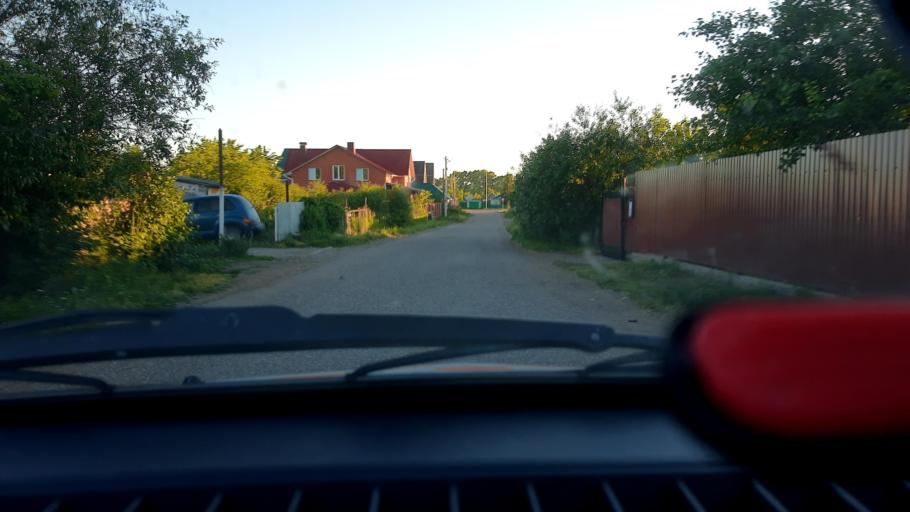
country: RU
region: Bashkortostan
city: Avdon
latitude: 54.4987
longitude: 55.8970
